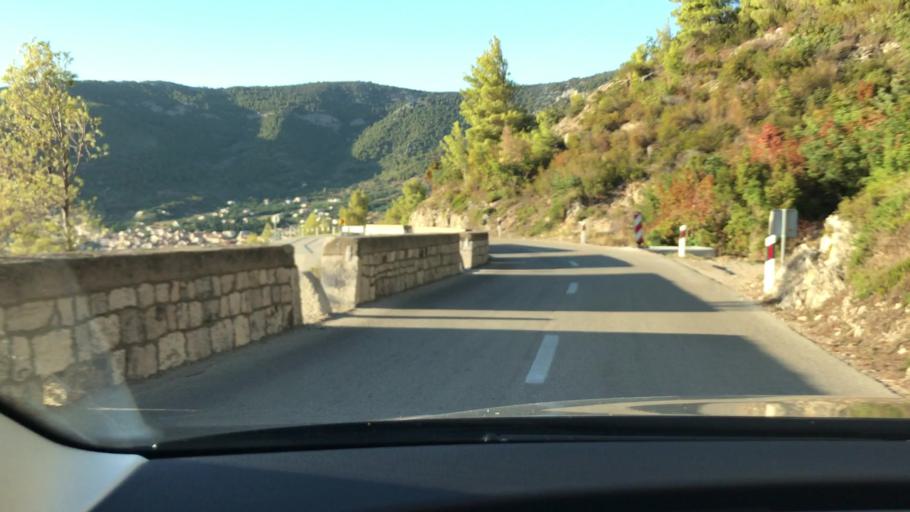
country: HR
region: Splitsko-Dalmatinska
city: Komiza
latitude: 43.0336
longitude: 16.0947
